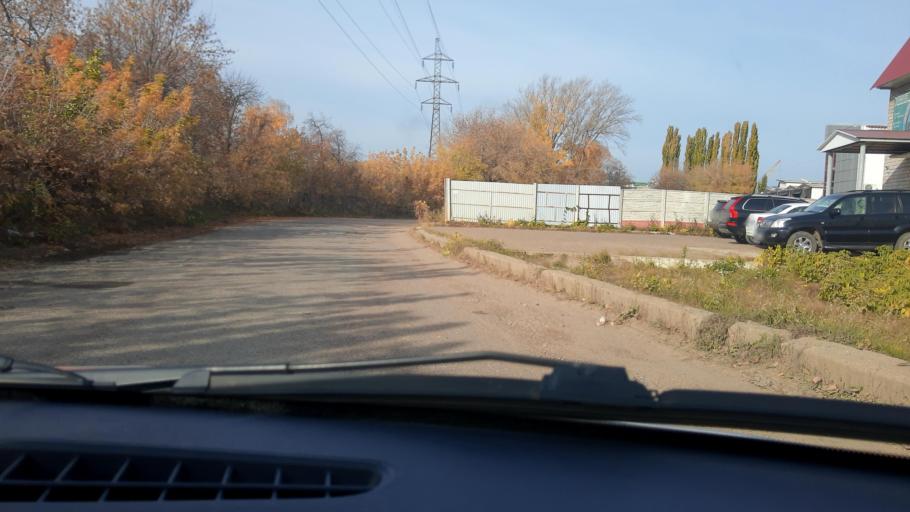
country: RU
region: Bashkortostan
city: Ufa
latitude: 54.7934
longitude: 56.0859
